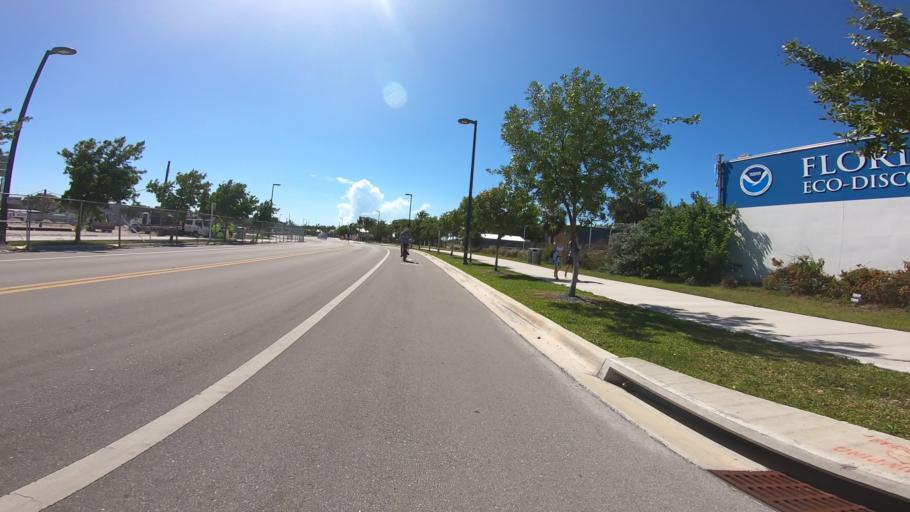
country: US
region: Florida
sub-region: Monroe County
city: Key West
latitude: 24.5489
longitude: -81.8059
